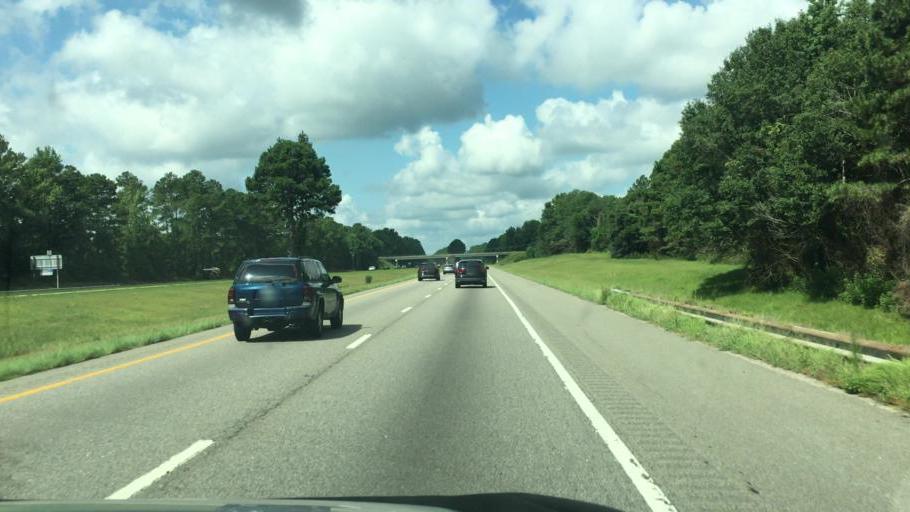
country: US
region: North Carolina
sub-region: Robeson County
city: Rowland
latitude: 34.5366
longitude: -79.2455
